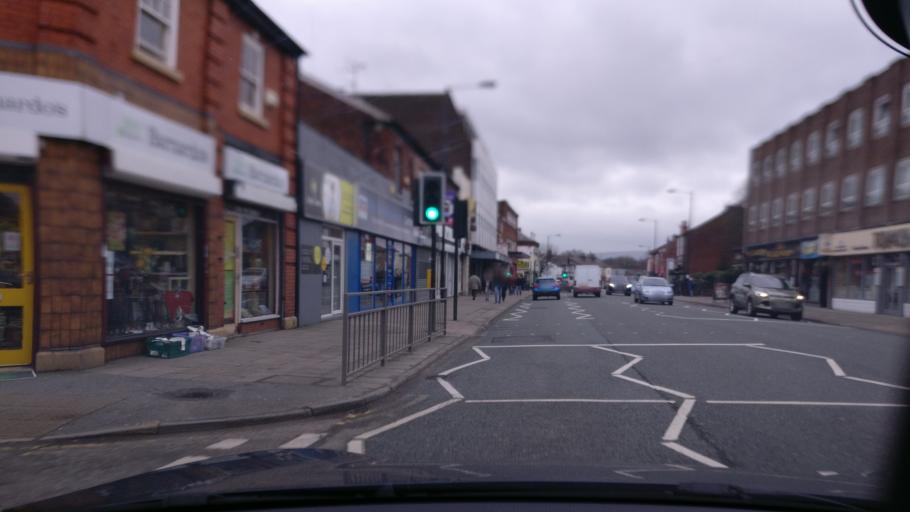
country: GB
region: England
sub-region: Borough of Stockport
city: Hazel Grove
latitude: 53.3797
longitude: -2.1210
